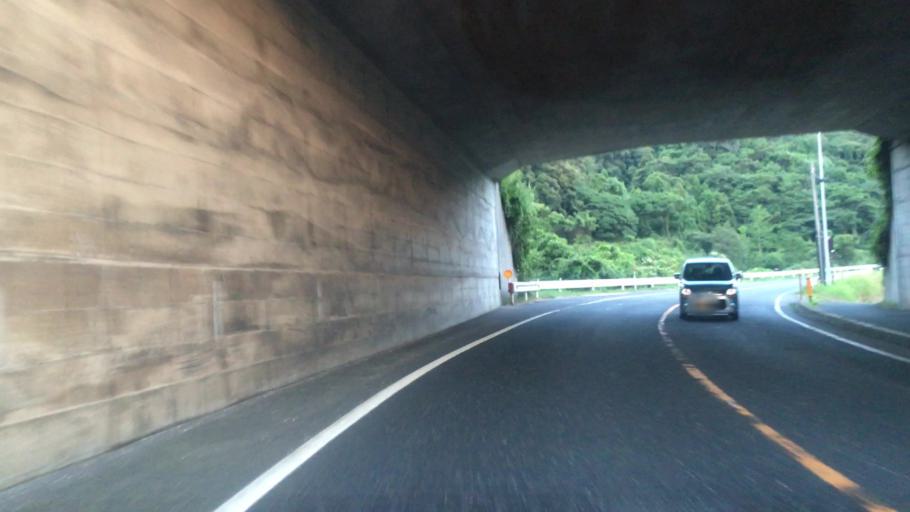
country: JP
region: Tottori
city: Tottori
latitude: 35.5995
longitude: 134.3516
